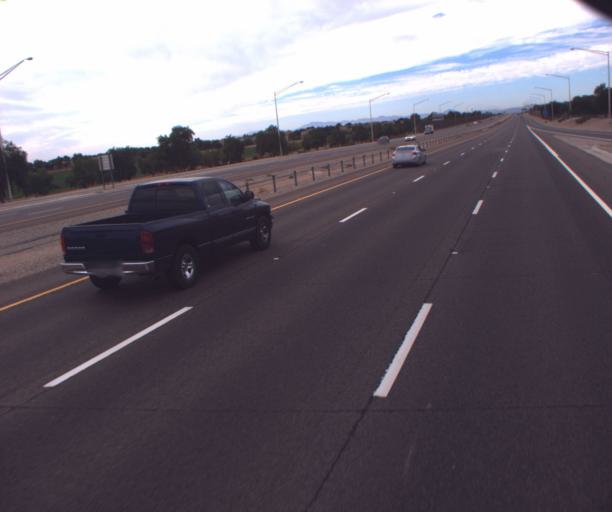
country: US
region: Arizona
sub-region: Maricopa County
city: Queen Creek
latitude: 33.3285
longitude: -111.6905
